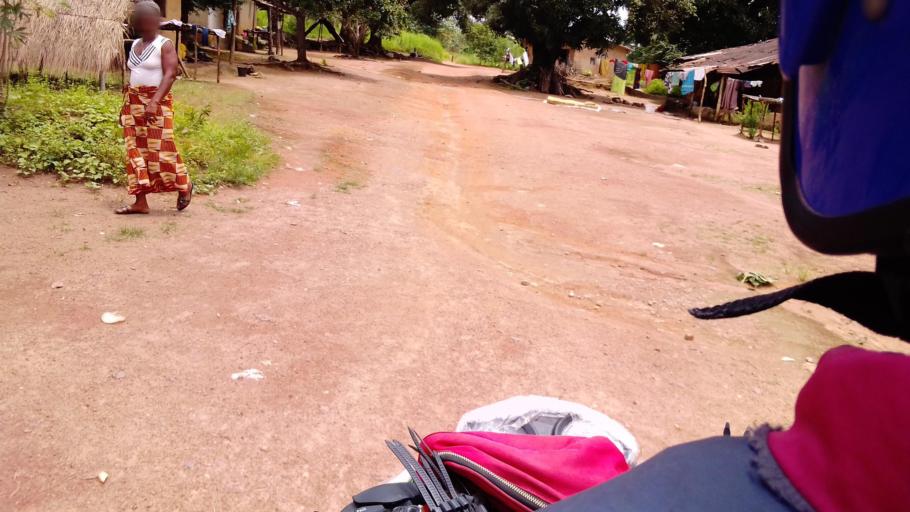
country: SL
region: Eastern Province
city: Koidu
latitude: 8.6775
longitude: -10.9563
